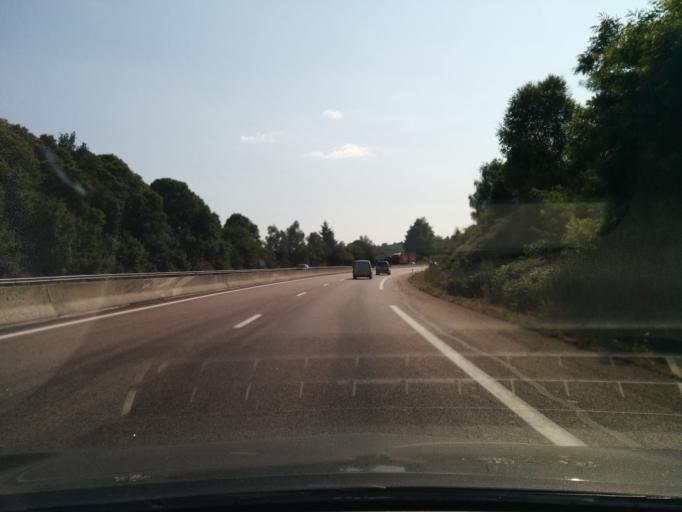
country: FR
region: Limousin
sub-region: Departement de la Haute-Vienne
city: Razes
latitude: 45.9940
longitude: 1.3349
